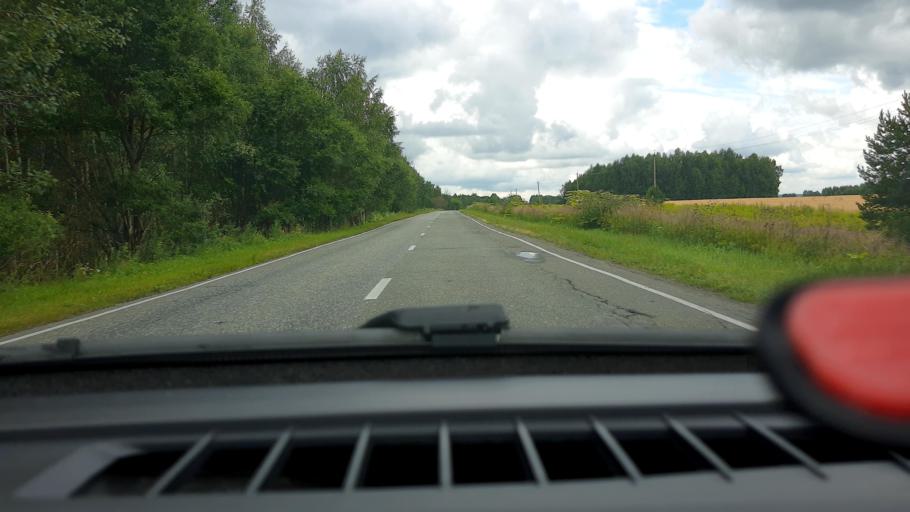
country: RU
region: Nizjnij Novgorod
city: Neklyudovo
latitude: 56.5206
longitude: 43.8868
